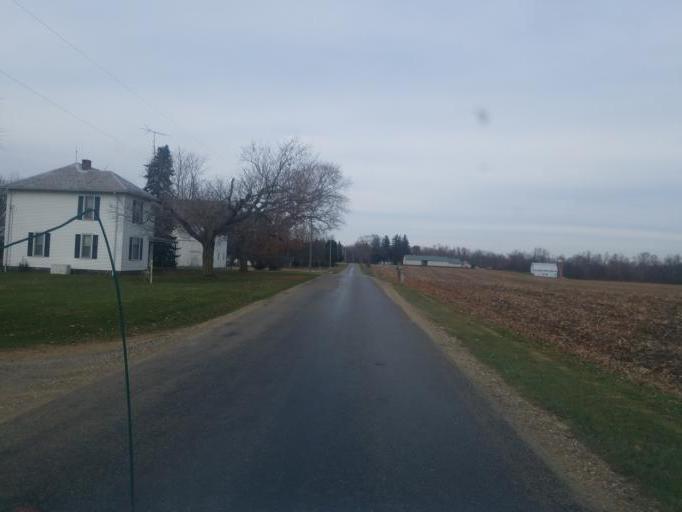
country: US
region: Ohio
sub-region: Knox County
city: Mount Vernon
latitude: 40.4141
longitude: -82.5131
